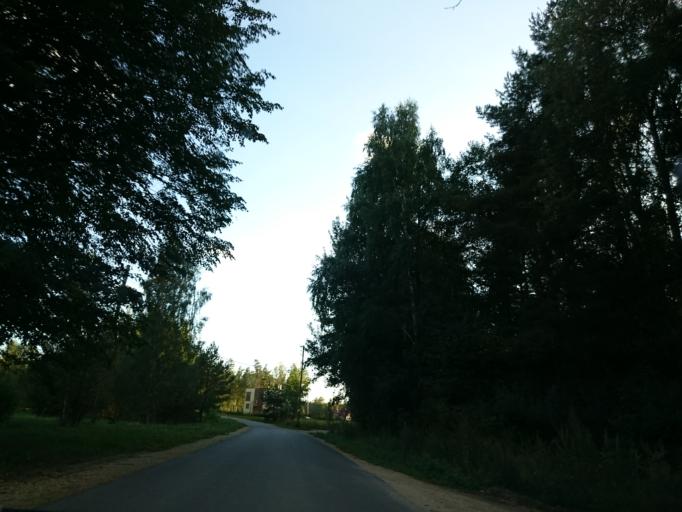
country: LV
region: Adazi
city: Adazi
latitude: 57.0695
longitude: 24.2706
